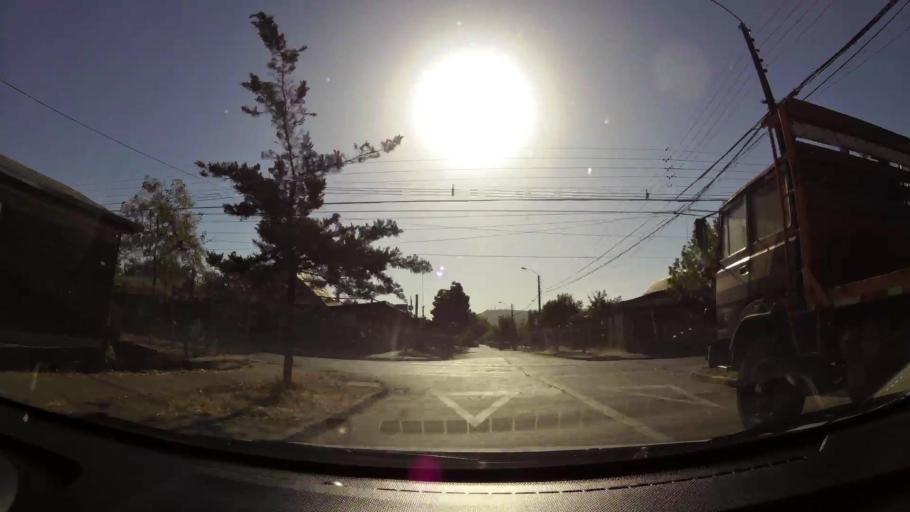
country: CL
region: Maule
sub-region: Provincia de Talca
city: Talca
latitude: -35.4176
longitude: -71.6503
